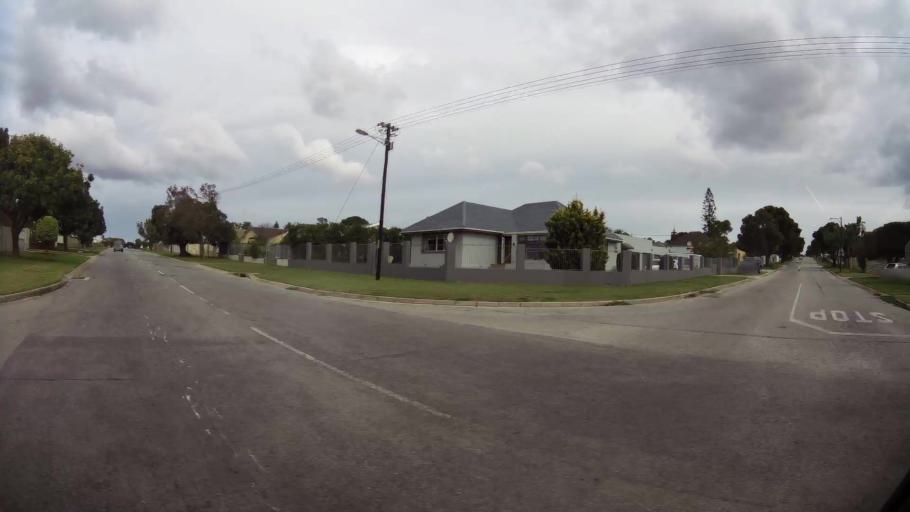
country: ZA
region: Eastern Cape
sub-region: Nelson Mandela Bay Metropolitan Municipality
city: Port Elizabeth
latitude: -33.9389
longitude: 25.5192
